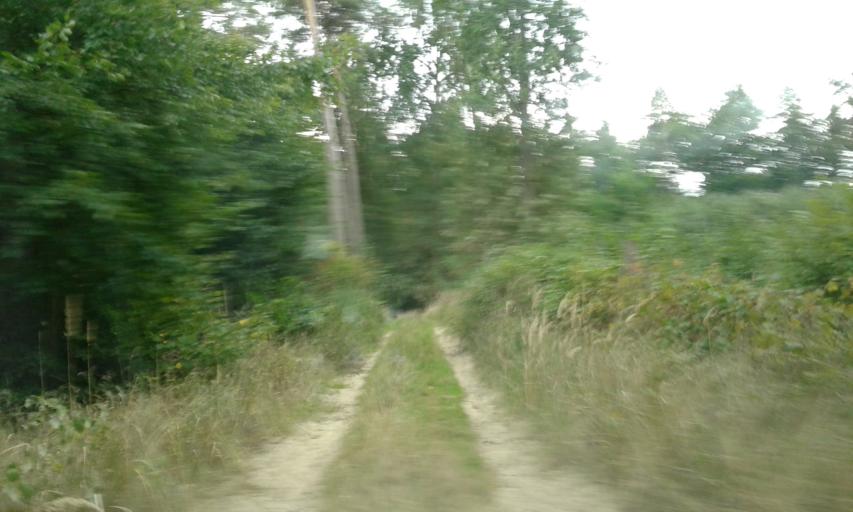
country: PL
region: West Pomeranian Voivodeship
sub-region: Powiat stargardzki
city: Dolice
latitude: 53.1804
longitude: 15.1495
